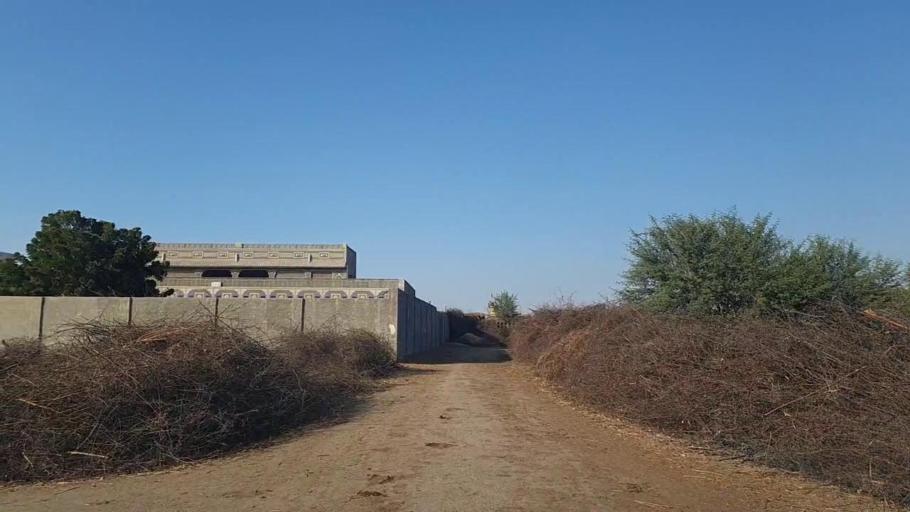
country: PK
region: Sindh
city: Shahpur Chakar
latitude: 26.1968
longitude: 68.6362
